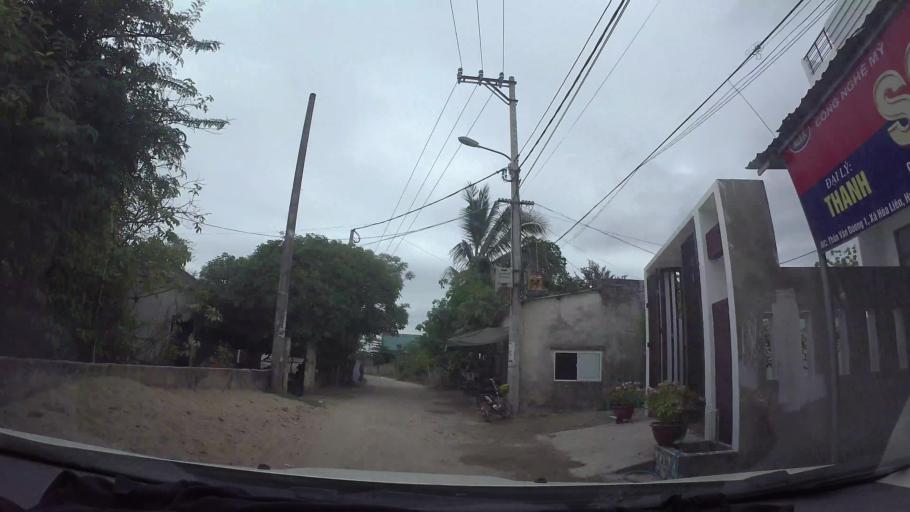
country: VN
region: Da Nang
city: Lien Chieu
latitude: 16.0897
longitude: 108.1055
